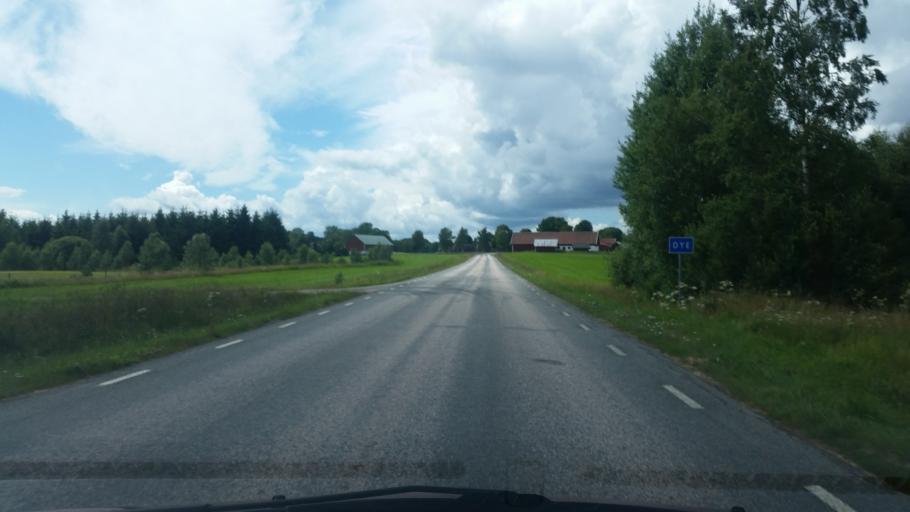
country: SE
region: Joenkoeping
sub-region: Gislaveds Kommun
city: Reftele
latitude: 57.2091
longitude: 13.6105
